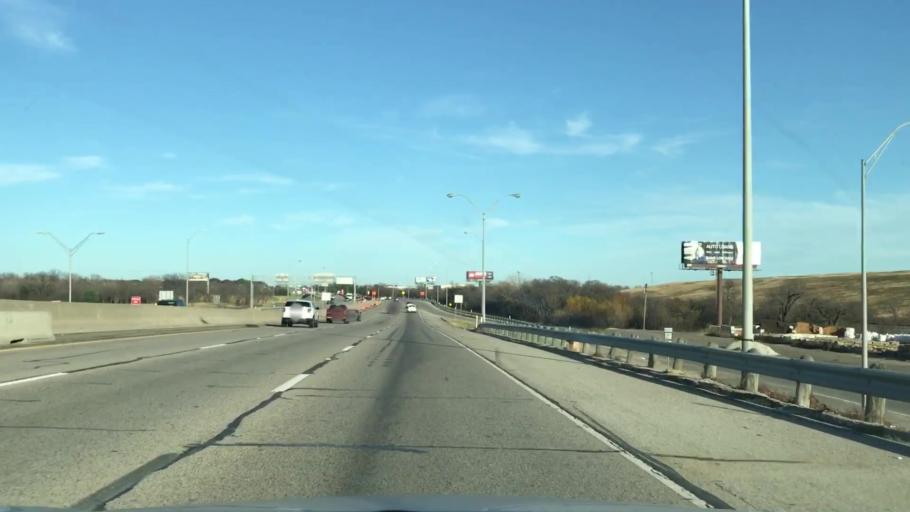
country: US
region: Texas
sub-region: Tarrant County
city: Haltom City
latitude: 32.7924
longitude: -97.2432
